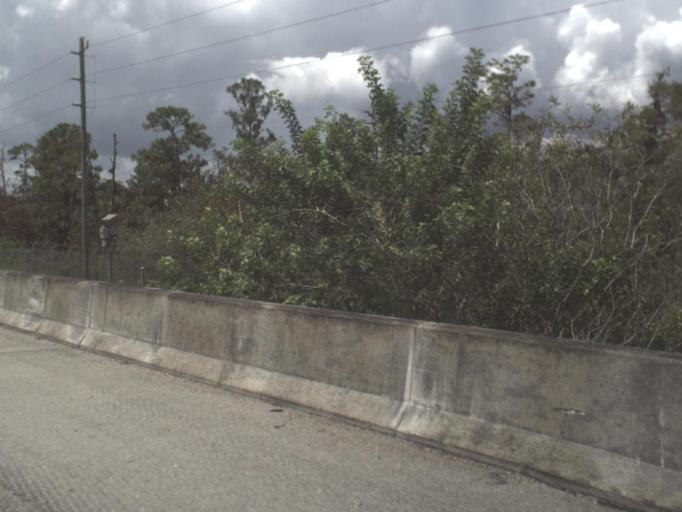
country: US
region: Florida
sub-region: Collier County
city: Immokalee
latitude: 26.1553
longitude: -81.3106
